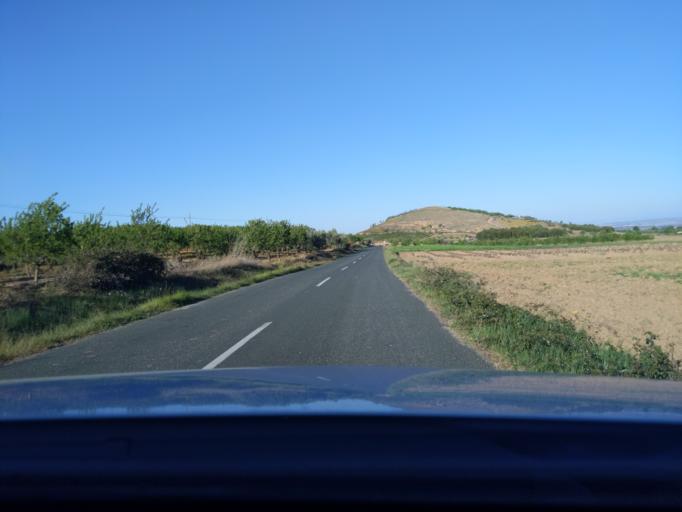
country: ES
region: La Rioja
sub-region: Provincia de La Rioja
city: Bergasa
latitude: 42.2675
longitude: -2.1019
